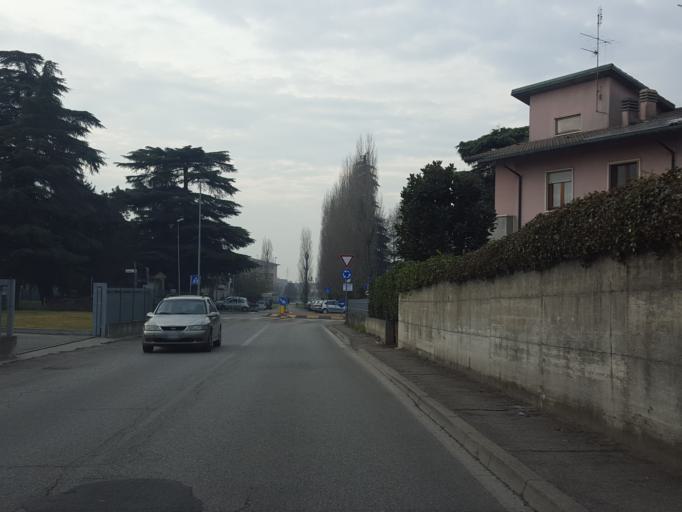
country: IT
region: Veneto
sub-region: Provincia di Verona
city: San Bonifacio
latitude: 45.3967
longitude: 11.2835
